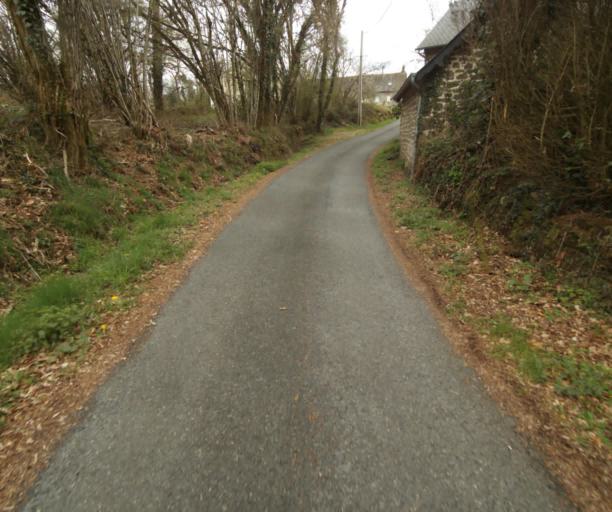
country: FR
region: Limousin
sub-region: Departement de la Correze
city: Correze
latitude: 45.3292
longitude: 1.9359
